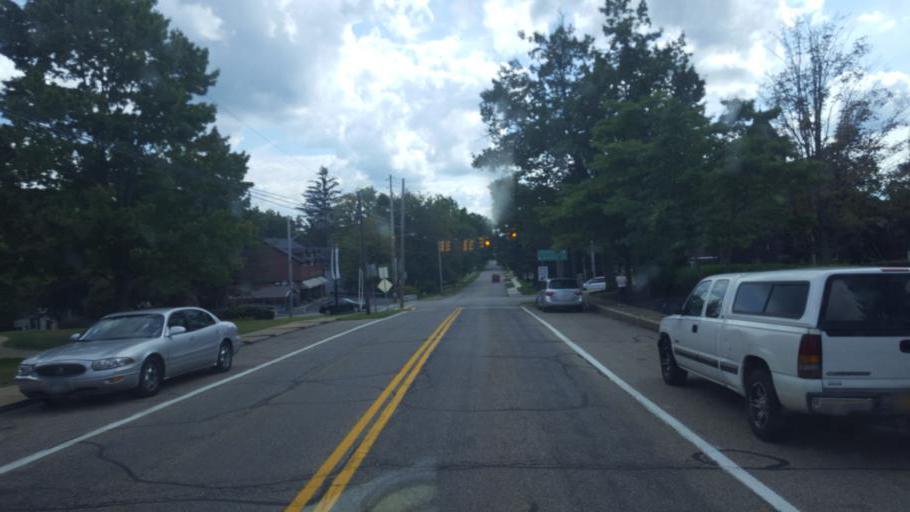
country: US
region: Ohio
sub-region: Portage County
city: Hiram
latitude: 41.3100
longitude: -81.1436
